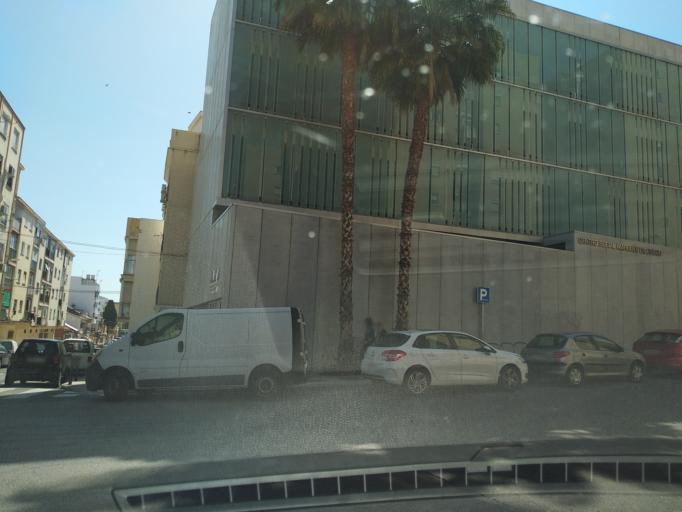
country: ES
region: Andalusia
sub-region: Provincia de Malaga
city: Malaga
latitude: 36.7288
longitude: -4.4382
